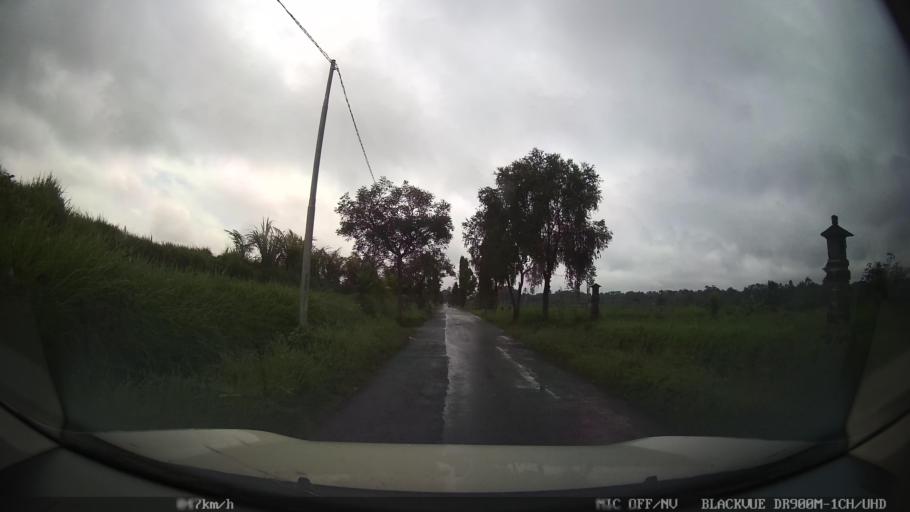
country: ID
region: Bali
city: Banjar Teguan
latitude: -8.4987
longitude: 115.2256
